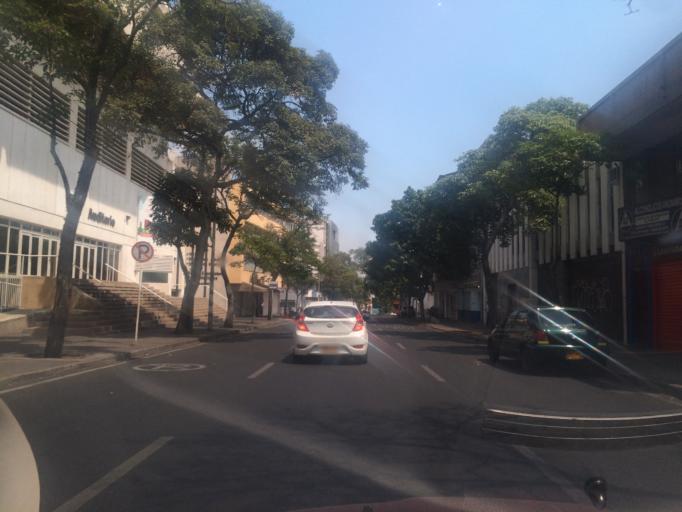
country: CO
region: Valle del Cauca
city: Cali
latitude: 3.4492
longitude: -76.5347
